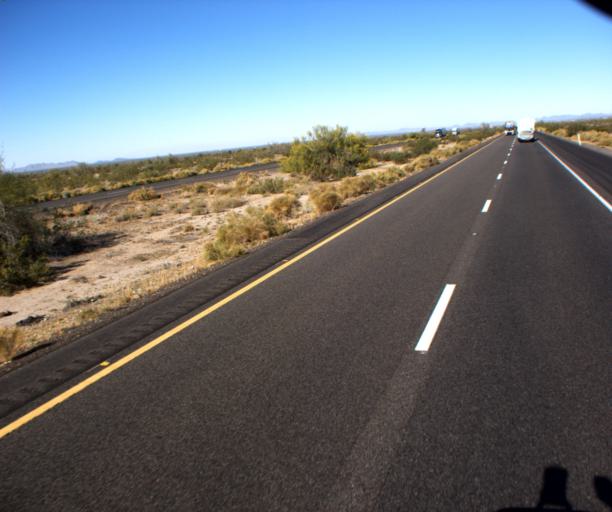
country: US
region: Arizona
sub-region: Maricopa County
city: Gila Bend
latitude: 32.9102
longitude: -112.6016
